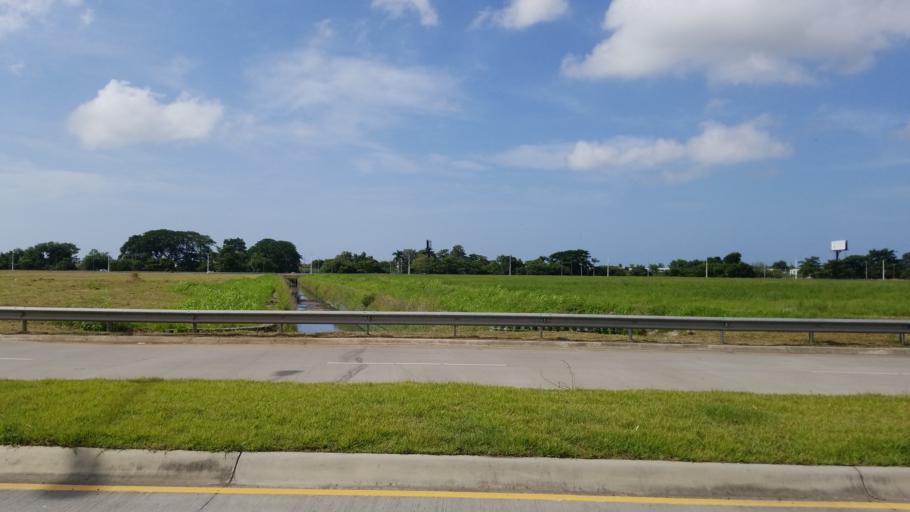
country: PA
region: Panama
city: San Miguelito
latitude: 9.0396
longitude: -79.4278
